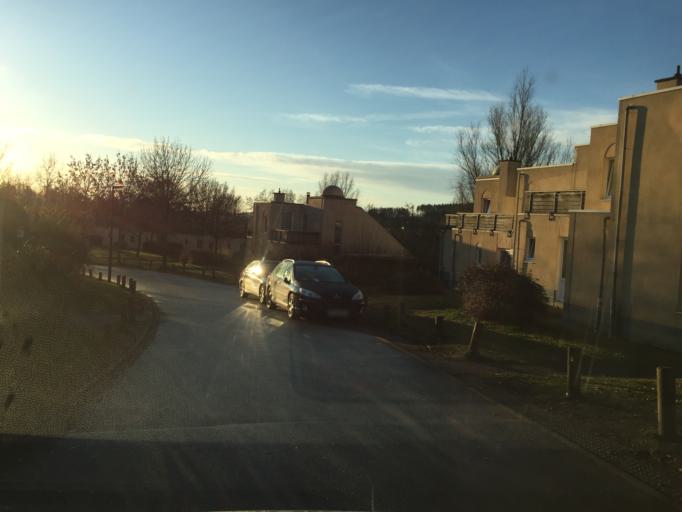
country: DE
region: North Rhine-Westphalia
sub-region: Regierungsbezirk Arnsberg
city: Medebach
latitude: 51.2088
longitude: 8.6855
